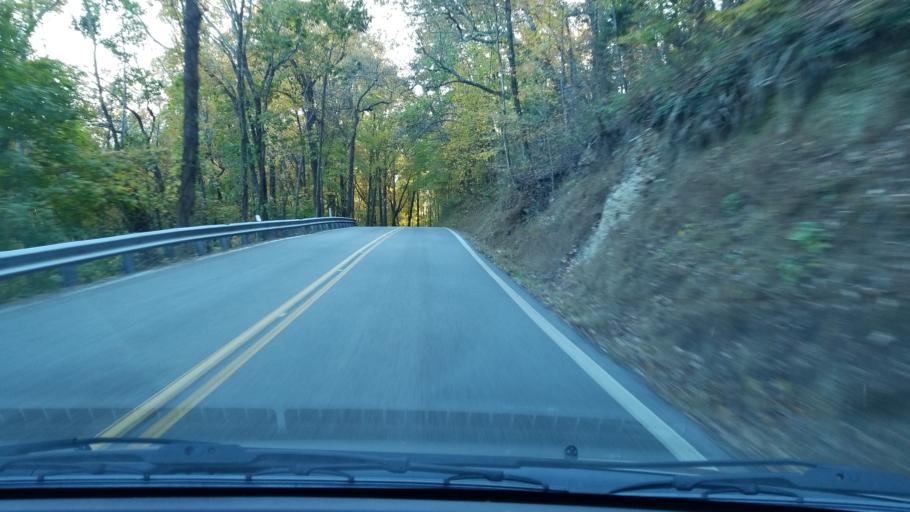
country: US
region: Tennessee
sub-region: Hamilton County
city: Falling Water
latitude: 35.2108
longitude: -85.2608
